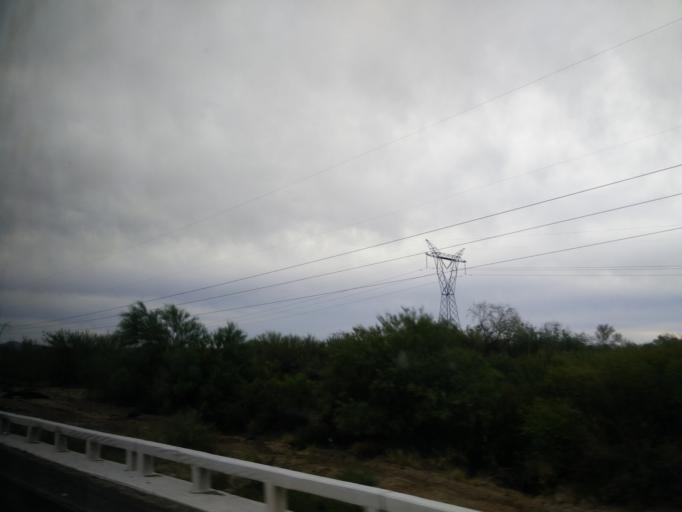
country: MX
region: Sonora
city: Hermosillo
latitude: 28.6686
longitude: -110.9958
